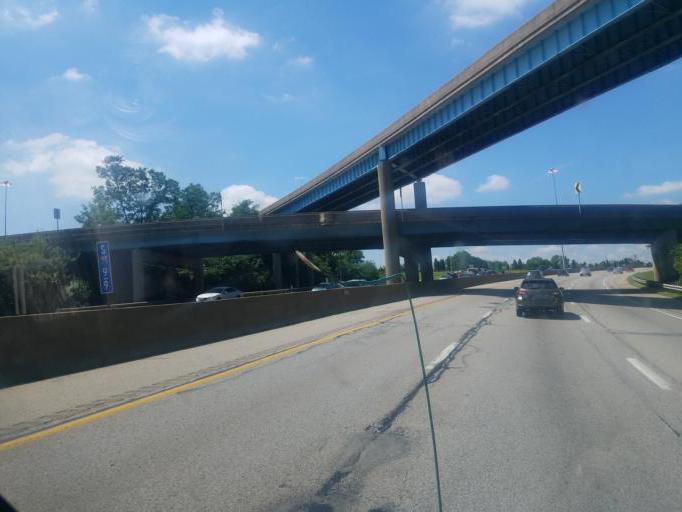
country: US
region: Ohio
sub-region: Hamilton County
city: Silverton
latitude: 39.1734
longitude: -84.3995
